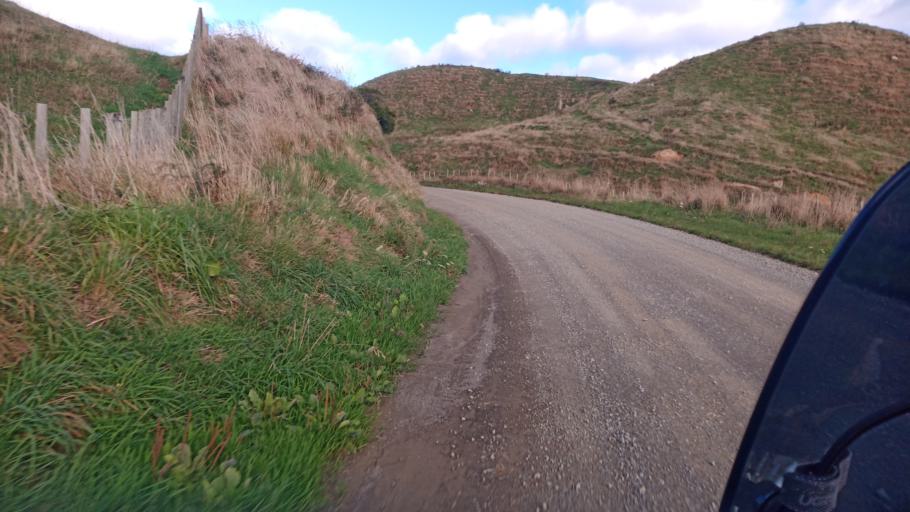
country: NZ
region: Bay of Plenty
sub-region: Opotiki District
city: Opotiki
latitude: -38.4540
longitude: 177.3949
